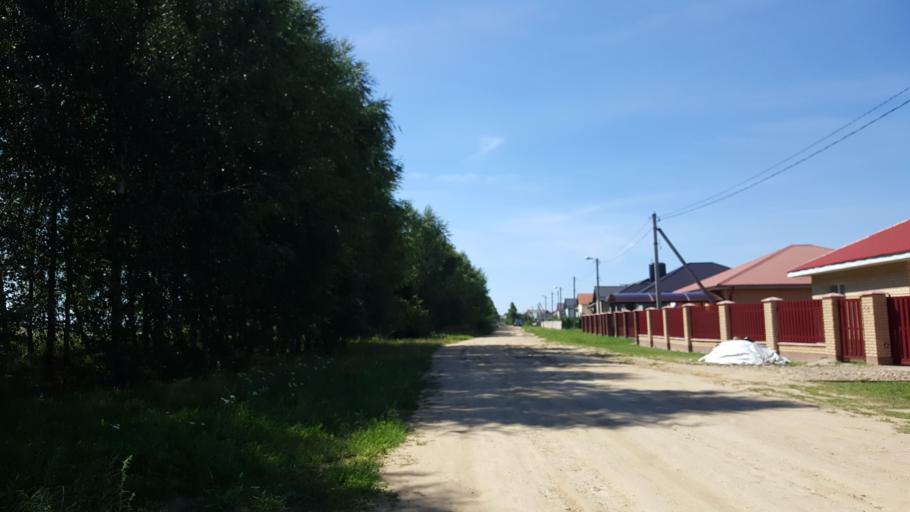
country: BY
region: Brest
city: Charnawchytsy
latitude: 52.2613
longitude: 23.5873
